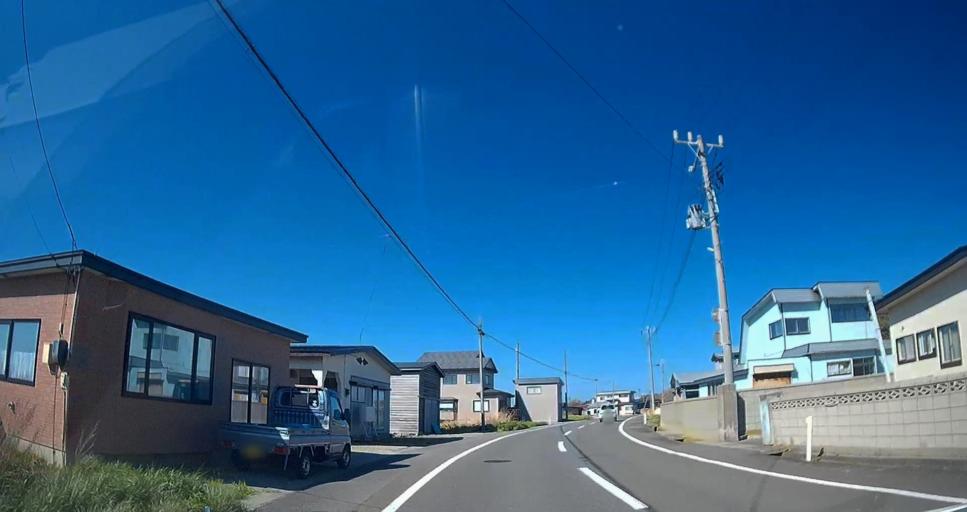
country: JP
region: Hokkaido
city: Hakodate
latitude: 41.5392
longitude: 140.9103
